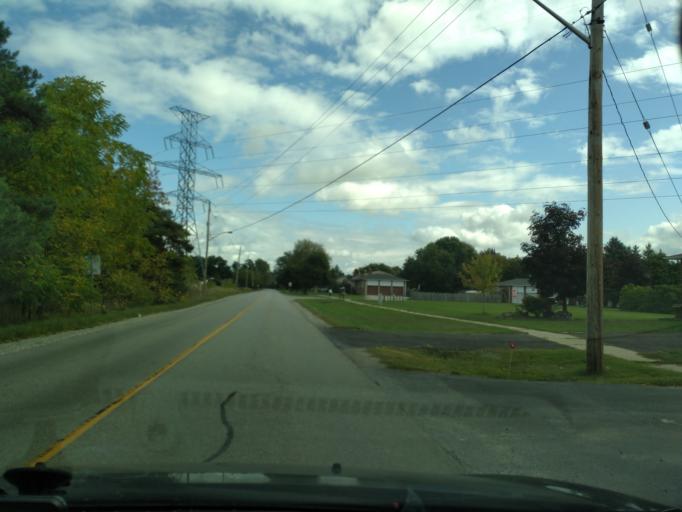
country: CA
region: Ontario
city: Newmarket
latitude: 44.1061
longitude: -79.5104
